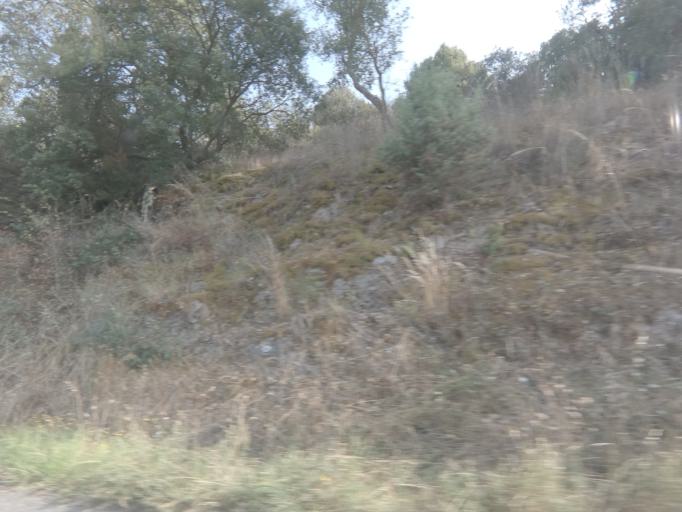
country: PT
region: Viseu
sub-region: Tabuaco
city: Tabuaco
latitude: 41.1317
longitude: -7.5400
